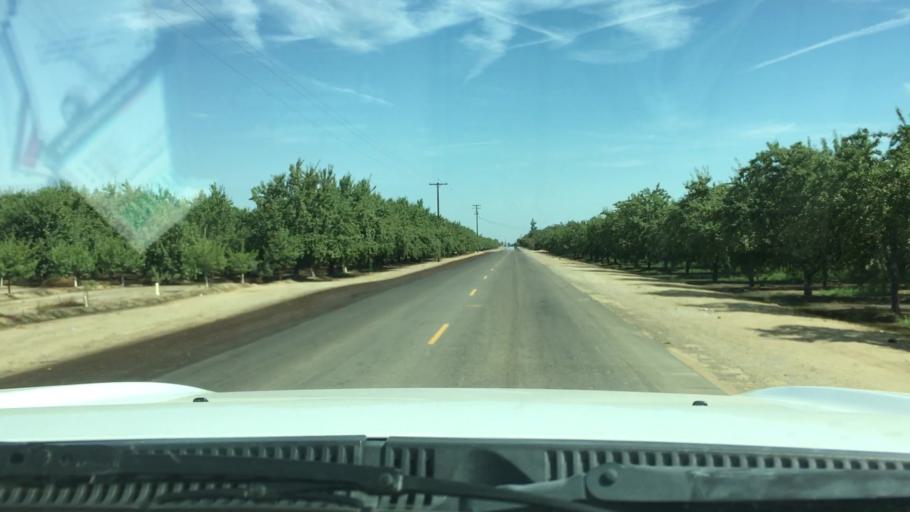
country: US
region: California
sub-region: Kern County
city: Shafter
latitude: 35.5050
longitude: -119.3501
